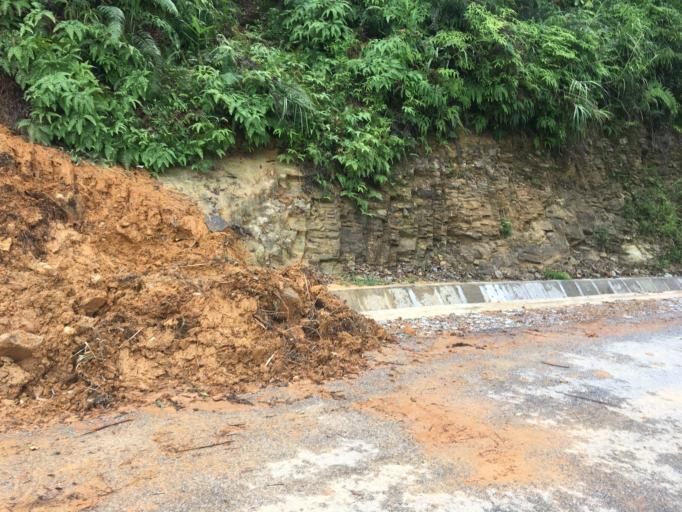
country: VN
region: Ha Giang
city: Thi Tran Tam Son
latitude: 22.9936
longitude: 105.0669
